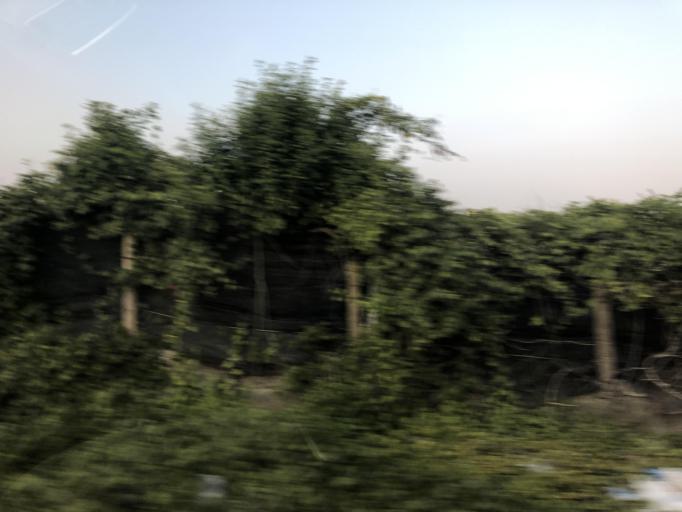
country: TW
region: Taiwan
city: Xinying
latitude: 23.1590
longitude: 120.2720
